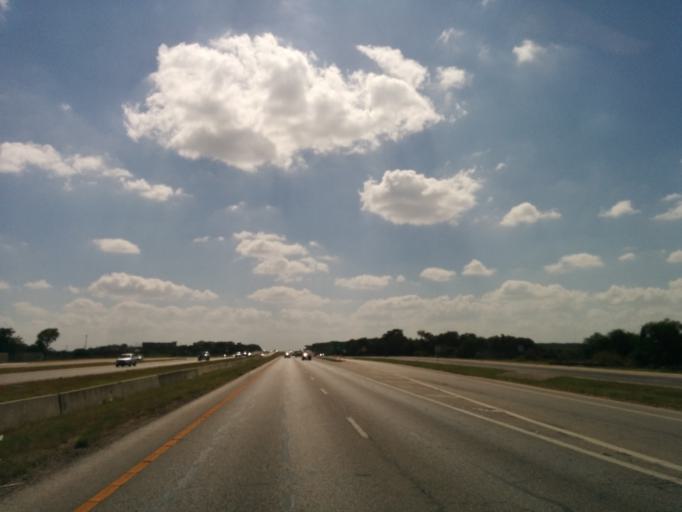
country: US
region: Texas
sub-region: Bexar County
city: Shavano Park
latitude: 29.6021
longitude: -98.5428
